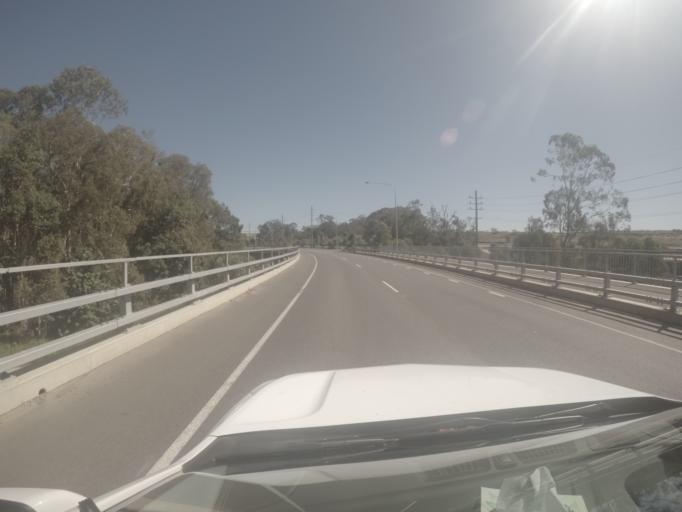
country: AU
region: Queensland
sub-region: Brisbane
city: Wacol
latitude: -27.5867
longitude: 152.9377
